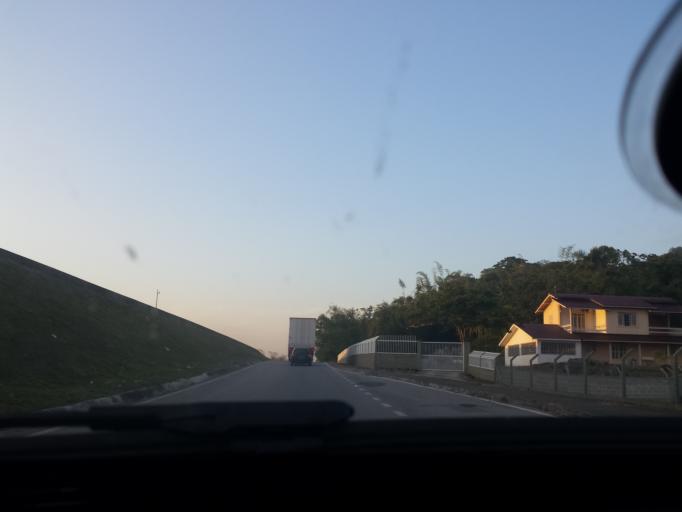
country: BR
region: Santa Catarina
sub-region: Florianopolis
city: Pantano do Sul
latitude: -27.8466
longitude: -48.6370
